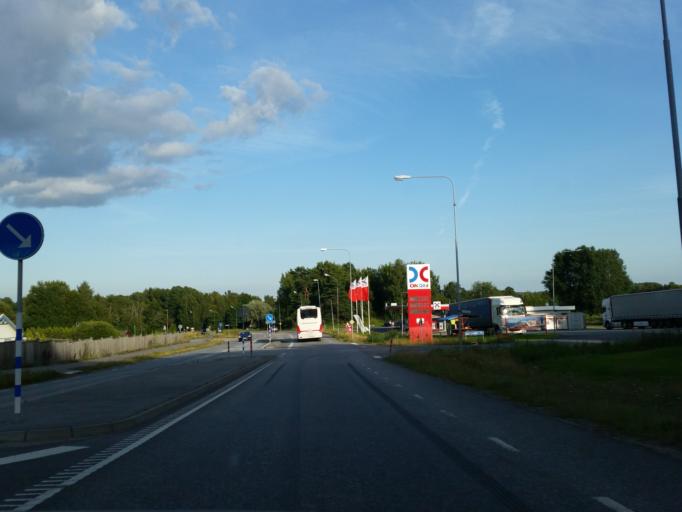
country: SE
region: Stockholm
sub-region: Sodertalje Kommun
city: Pershagen
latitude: 59.0879
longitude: 17.5770
